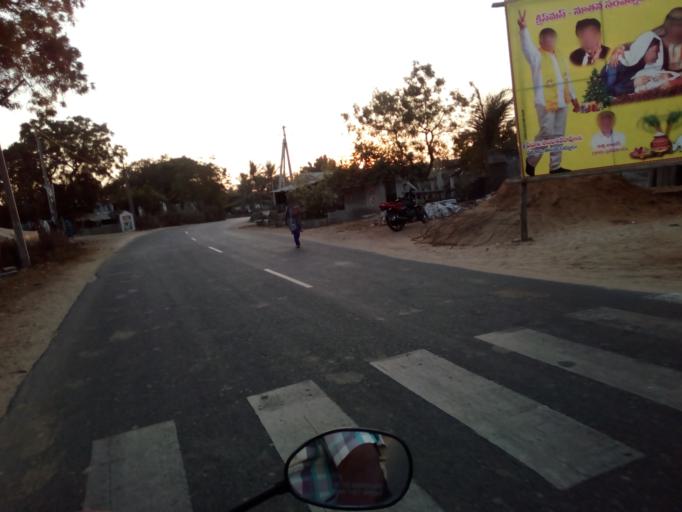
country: IN
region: Andhra Pradesh
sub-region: Prakasam
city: Vetapalem
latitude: 15.7281
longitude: 80.2560
